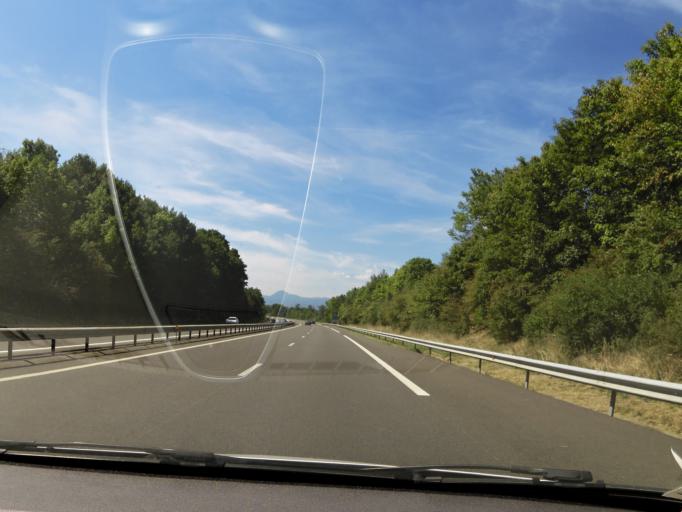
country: FR
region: Auvergne
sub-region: Departement du Puy-de-Dome
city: Culhat
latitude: 45.8400
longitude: 3.3150
